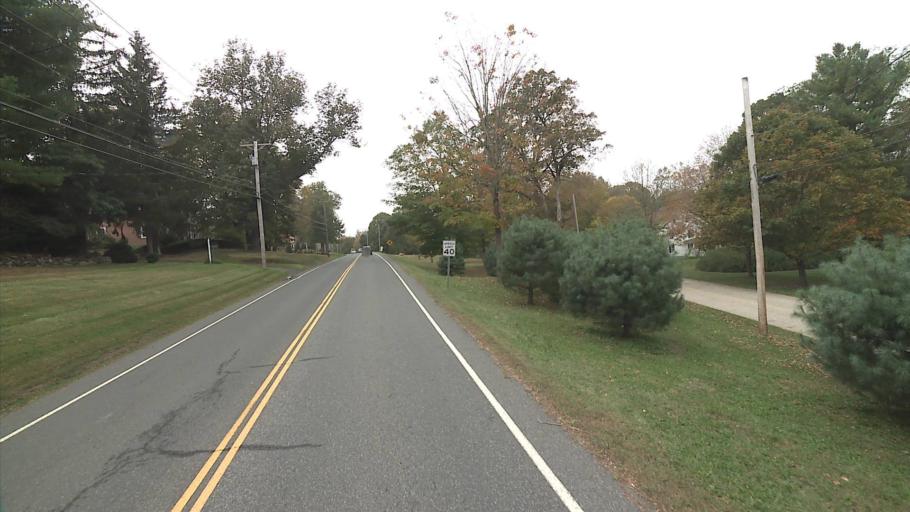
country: US
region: Connecticut
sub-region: New Haven County
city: Southbury
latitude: 41.5053
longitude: -73.2101
